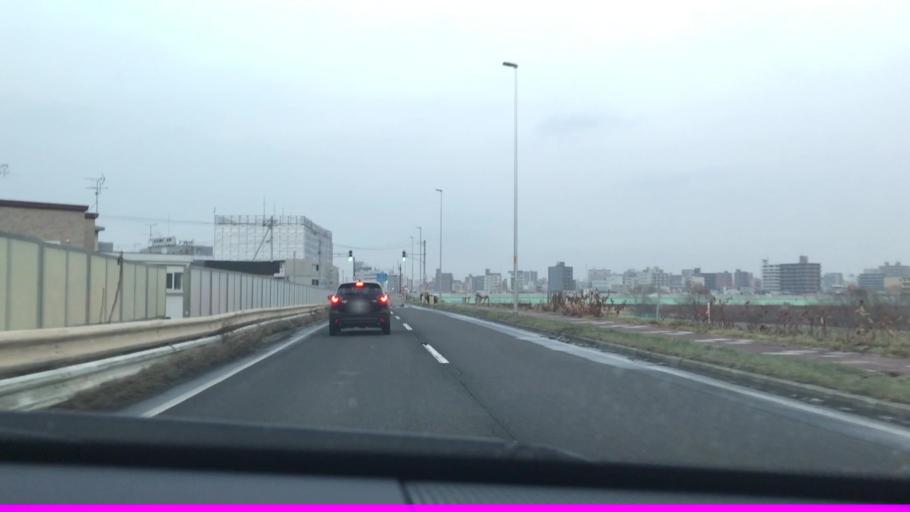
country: JP
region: Hokkaido
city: Sapporo
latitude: 43.0277
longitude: 141.3518
